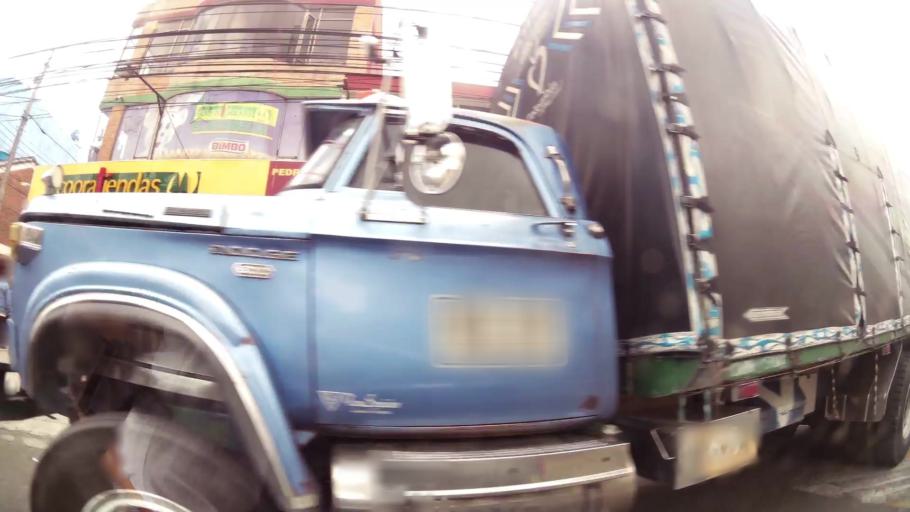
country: CO
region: Cundinamarca
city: Funza
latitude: 4.7029
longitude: -74.1178
